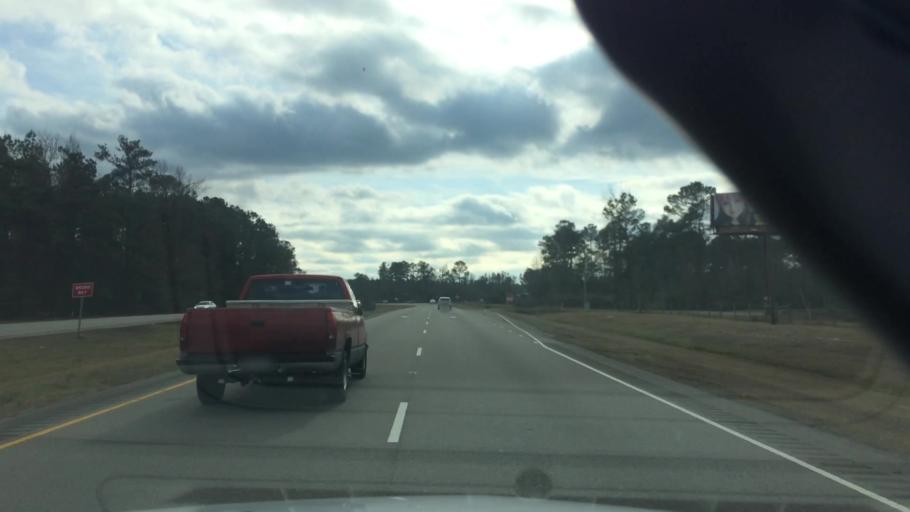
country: US
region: North Carolina
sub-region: Brunswick County
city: Bolivia
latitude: 34.1529
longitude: -78.0932
